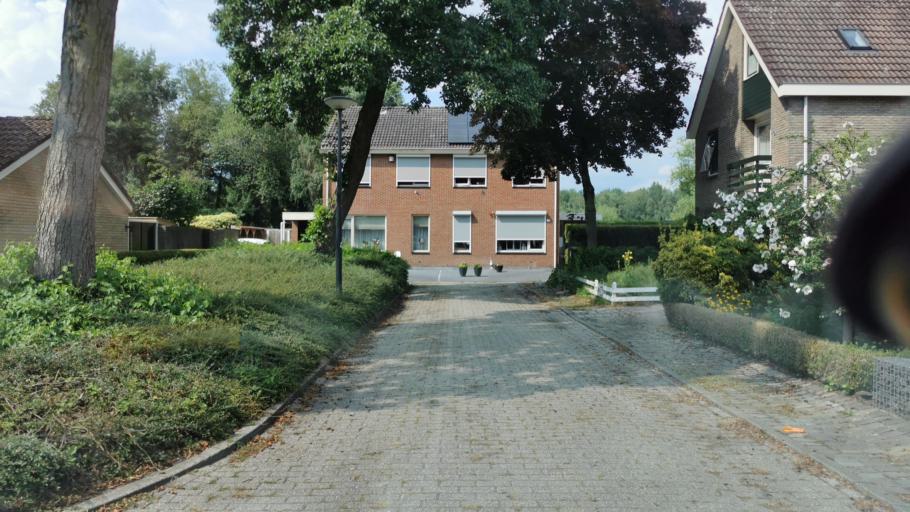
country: NL
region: Overijssel
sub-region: Gemeente Losser
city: Losser
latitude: 52.2224
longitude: 6.9653
